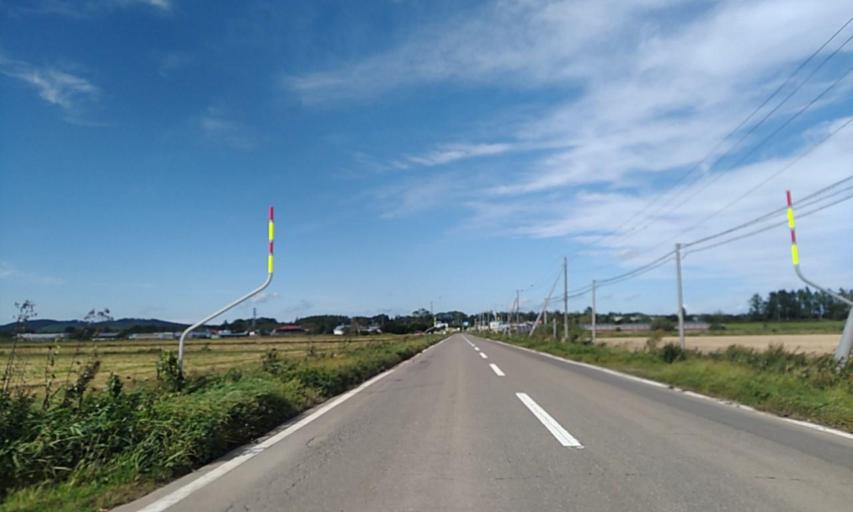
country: JP
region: Hokkaido
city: Obihiro
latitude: 42.7660
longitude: 143.6143
